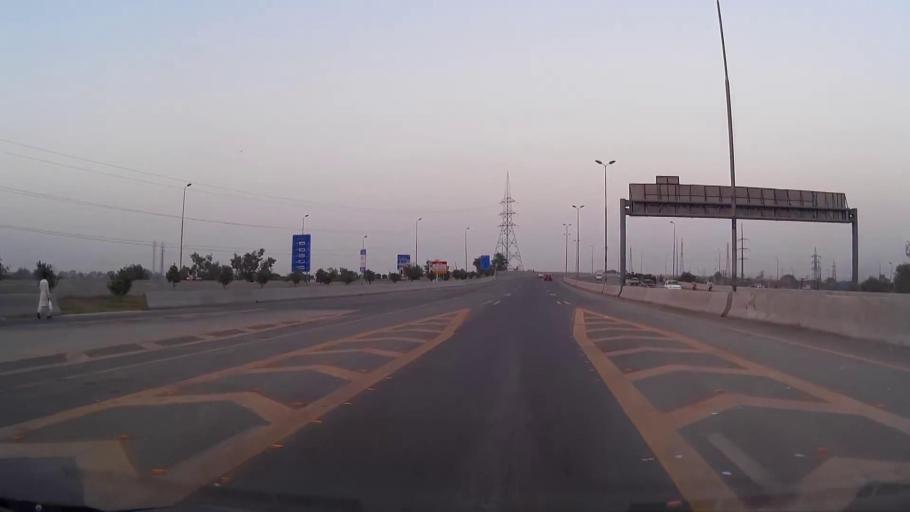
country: PK
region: Punjab
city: Lahore
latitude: 31.6094
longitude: 74.3040
